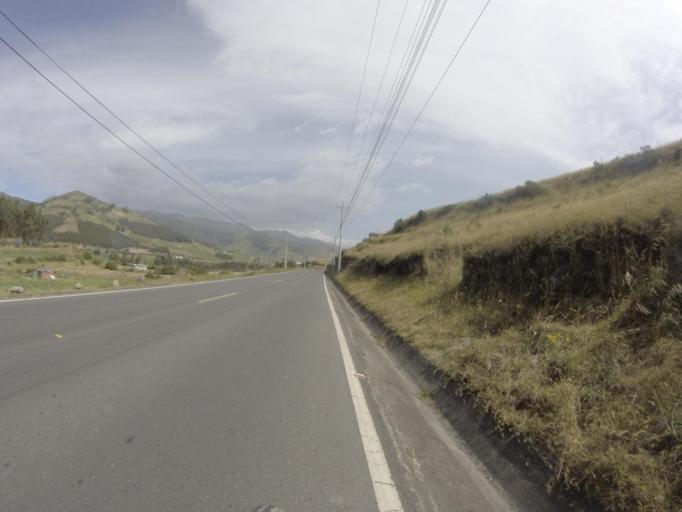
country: EC
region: Pichincha
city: Cayambe
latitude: 0.1262
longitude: -78.0817
